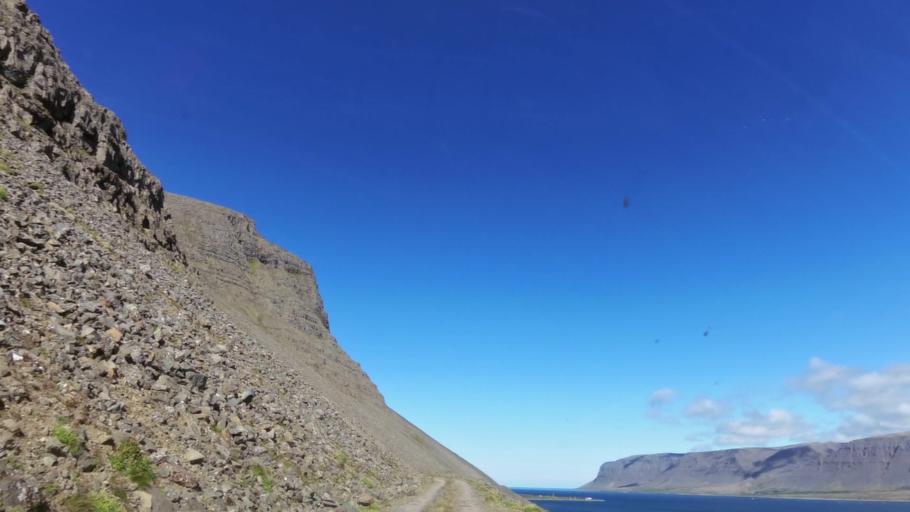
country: IS
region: West
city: Olafsvik
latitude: 65.6281
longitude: -23.9048
